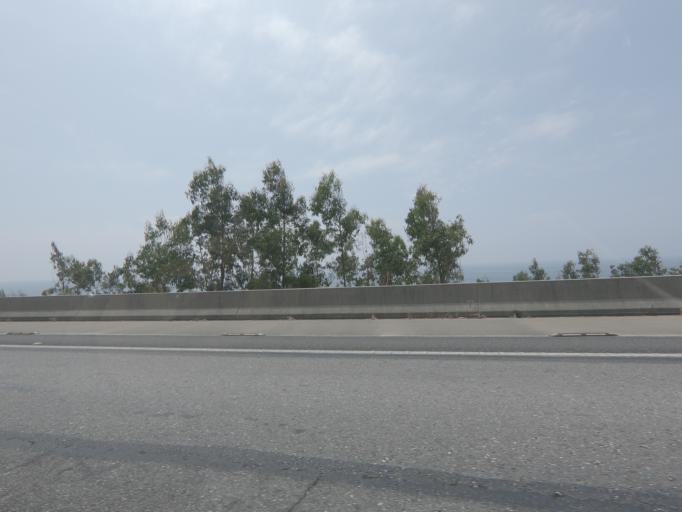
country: ES
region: Galicia
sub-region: Provincia de Pontevedra
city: A Guarda
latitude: 41.9344
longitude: -8.8837
